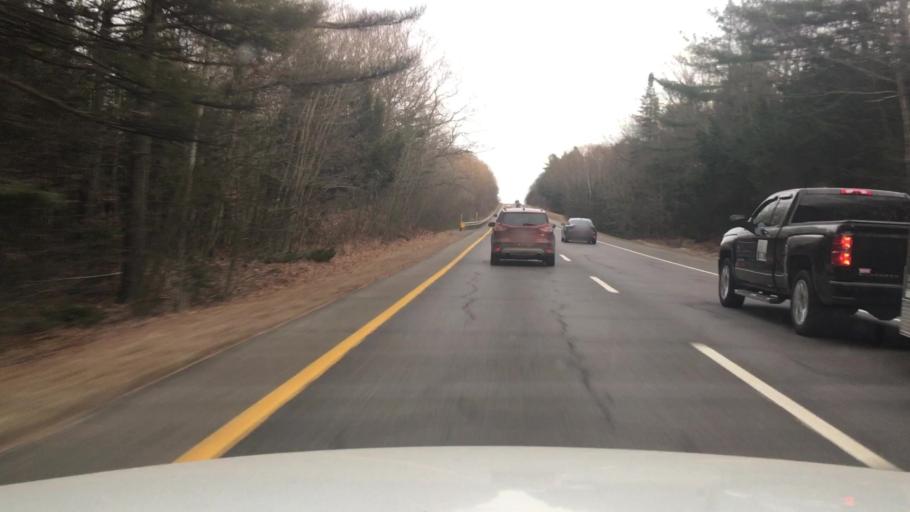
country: US
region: Maine
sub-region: Sagadahoc County
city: Bath
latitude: 43.9188
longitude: -69.8804
